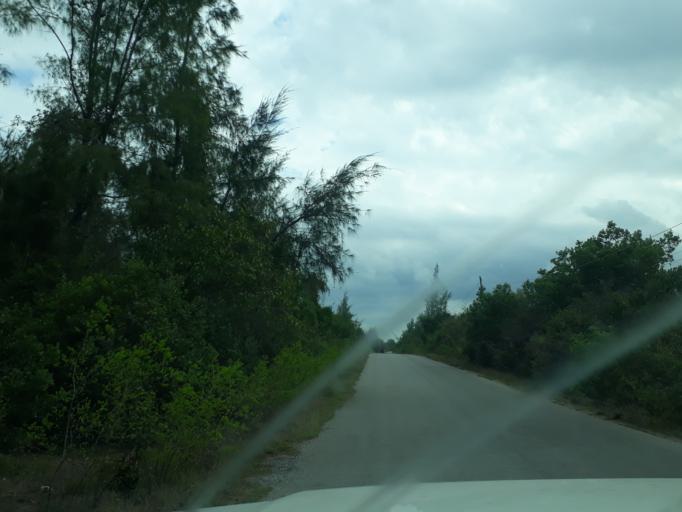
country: TZ
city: Kiwengwa
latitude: -6.0805
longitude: 39.4261
